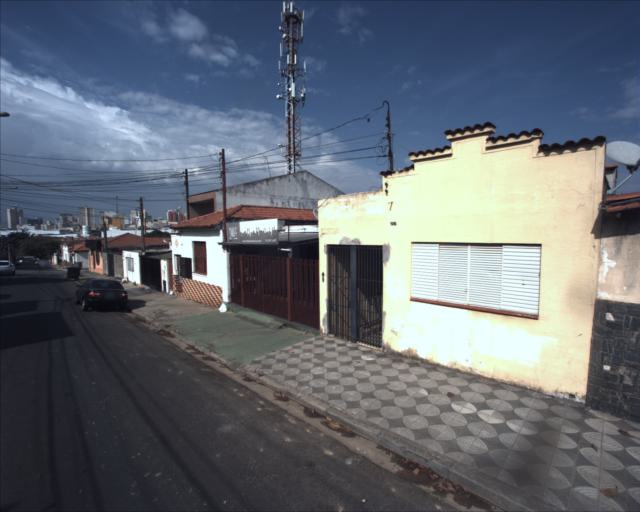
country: BR
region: Sao Paulo
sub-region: Sorocaba
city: Sorocaba
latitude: -23.4930
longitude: -47.4628
